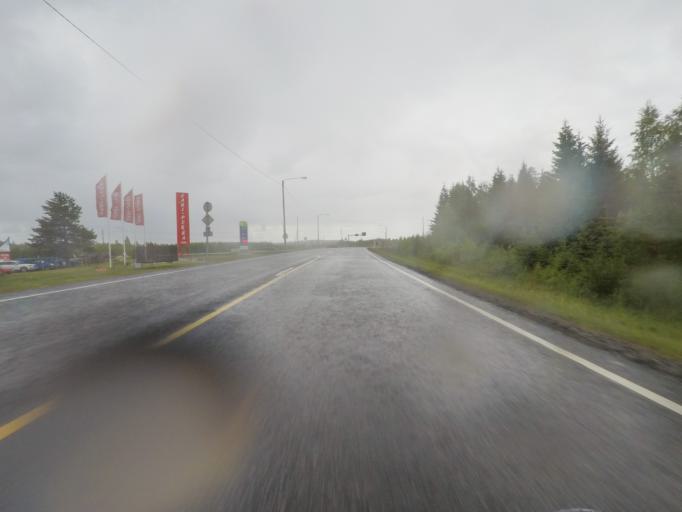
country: FI
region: Central Finland
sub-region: Jyvaeskylae
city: Hankasalmi
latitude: 62.3586
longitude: 26.5704
